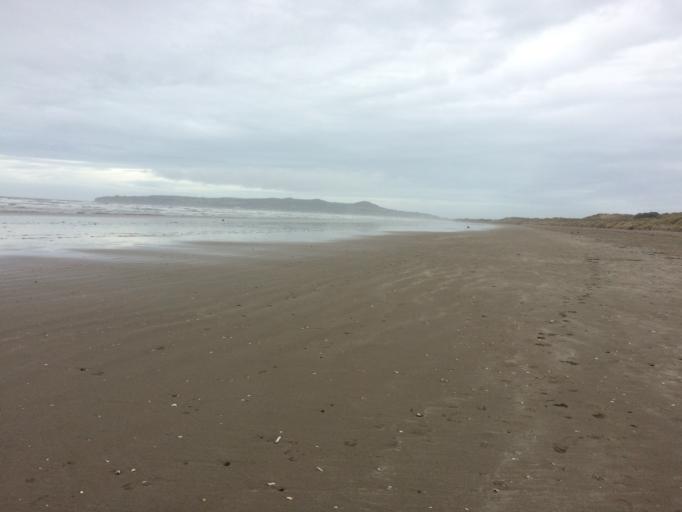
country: IE
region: Leinster
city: Portmarnock
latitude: 53.4242
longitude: -6.1225
